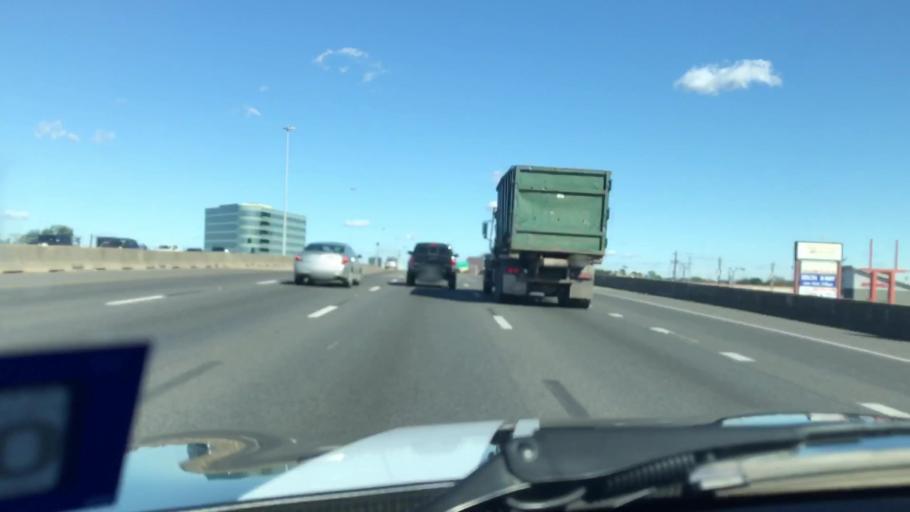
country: US
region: Texas
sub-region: Fort Bend County
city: Meadows Place
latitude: 29.6750
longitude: -95.5428
